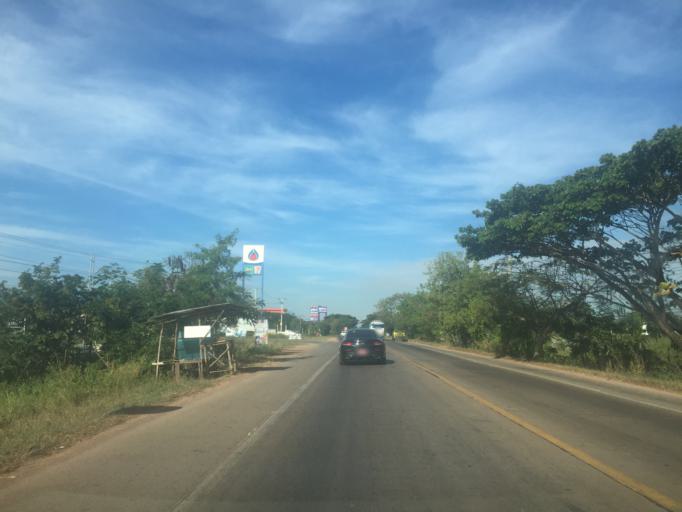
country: TH
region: Changwat Udon Thani
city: Kumphawapi
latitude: 17.1144
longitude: 102.9996
